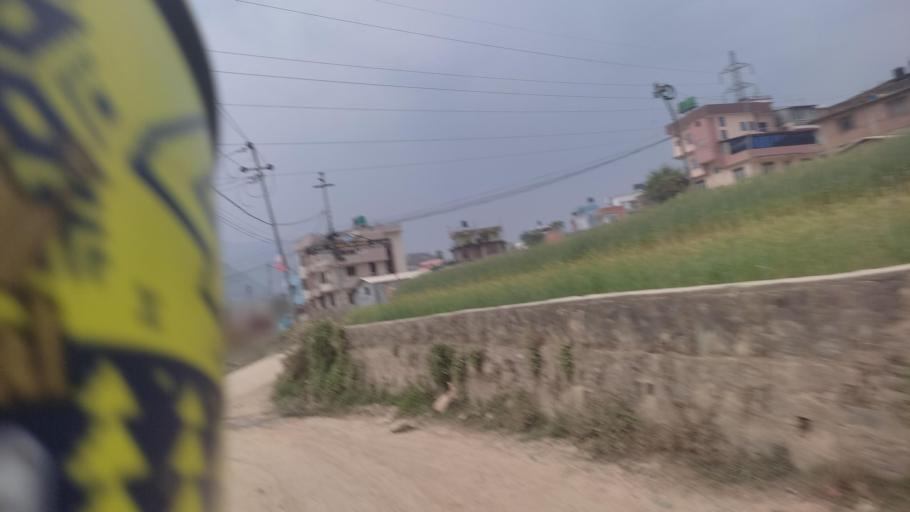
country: NP
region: Central Region
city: Kirtipur
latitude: 27.6633
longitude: 85.2712
